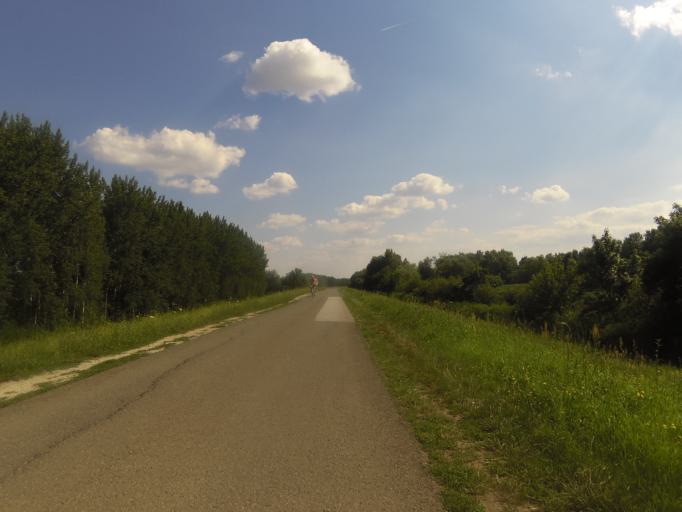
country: HU
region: Jasz-Nagykun-Szolnok
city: Tiszaszolos
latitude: 47.5905
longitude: 20.7109
